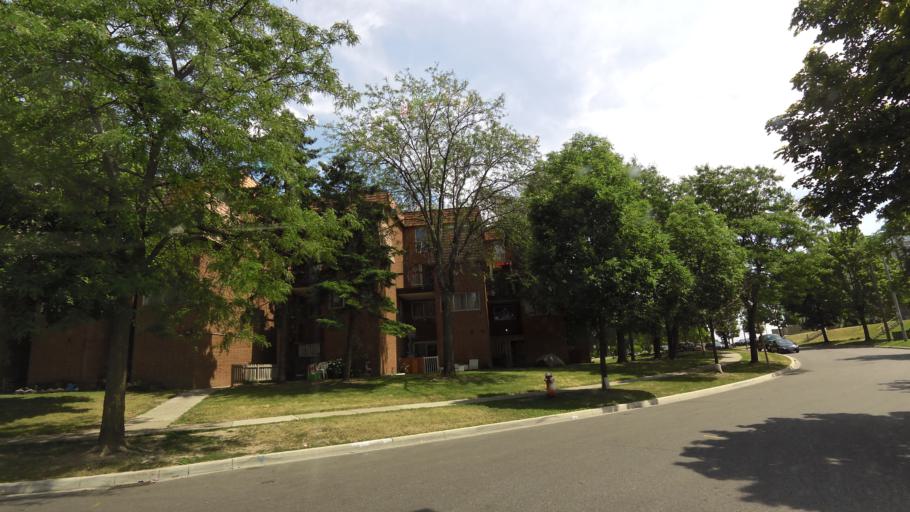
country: CA
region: Ontario
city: Etobicoke
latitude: 43.6197
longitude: -79.5967
